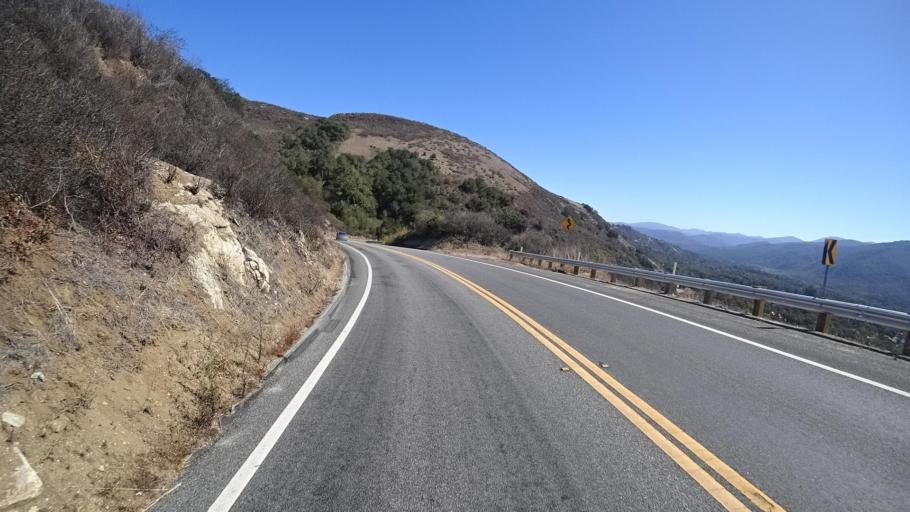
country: US
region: California
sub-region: Monterey County
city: Carmel Valley Village
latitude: 36.5158
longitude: -121.7573
